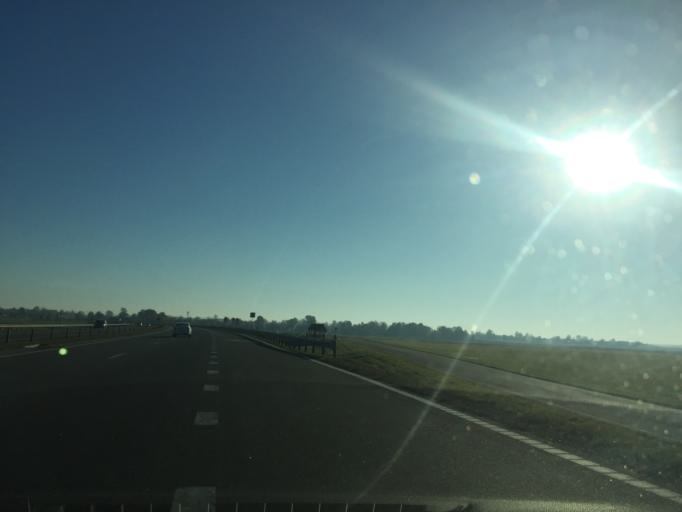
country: BY
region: Minsk
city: Smilavichy
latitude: 53.7583
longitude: 27.9625
